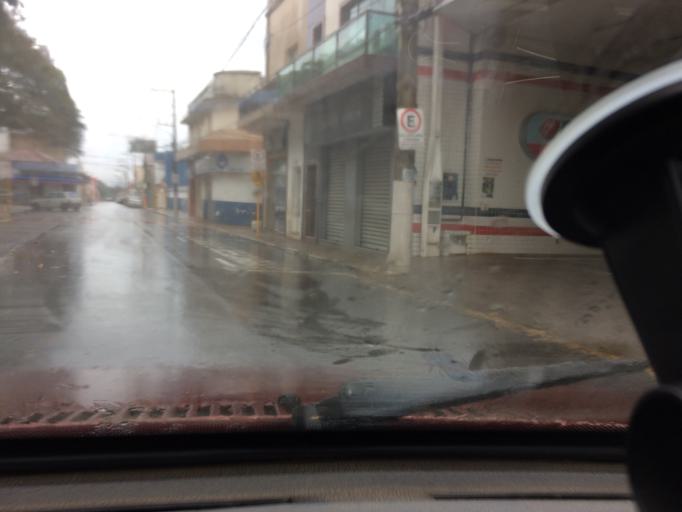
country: BR
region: Sao Paulo
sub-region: Capao Bonito
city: Capao Bonito
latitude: -24.0055
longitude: -48.3495
